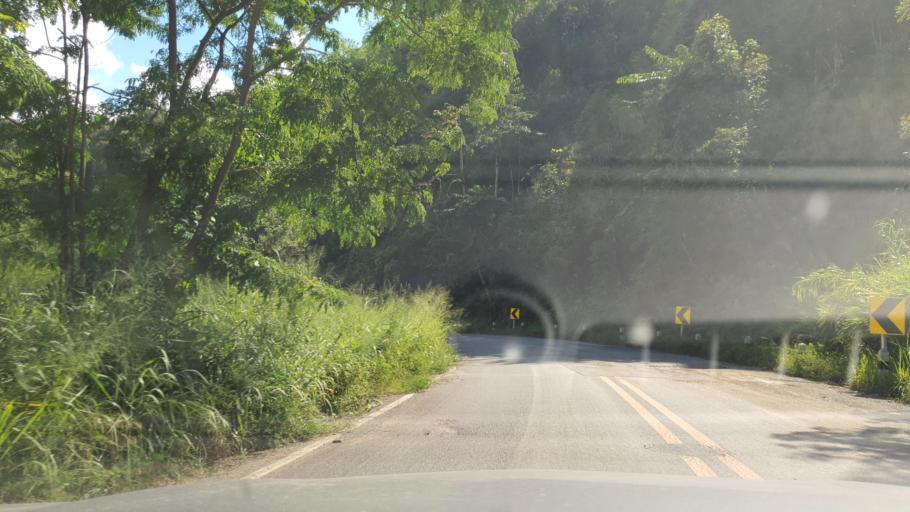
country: TH
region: Chiang Rai
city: Wiang Pa Pao
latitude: 19.3284
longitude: 99.4465
